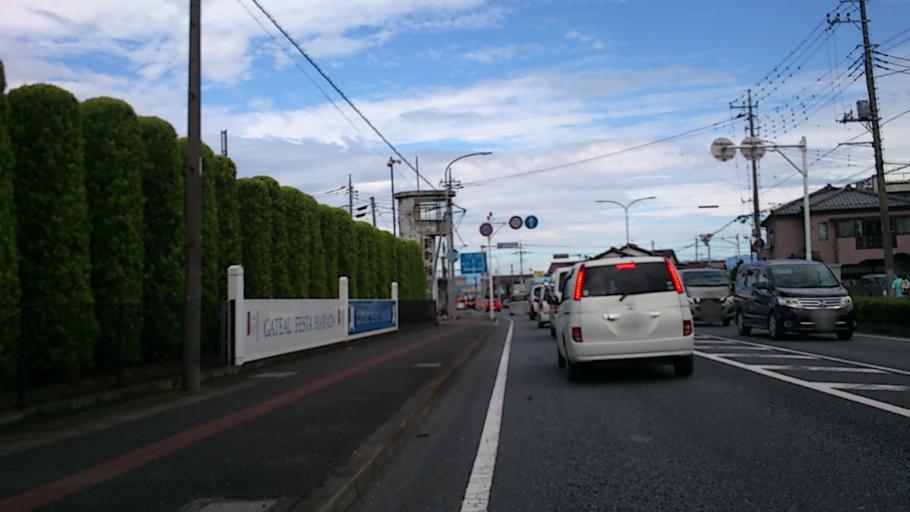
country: JP
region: Gunma
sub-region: Sawa-gun
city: Tamamura
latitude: 36.2700
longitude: 139.1147
